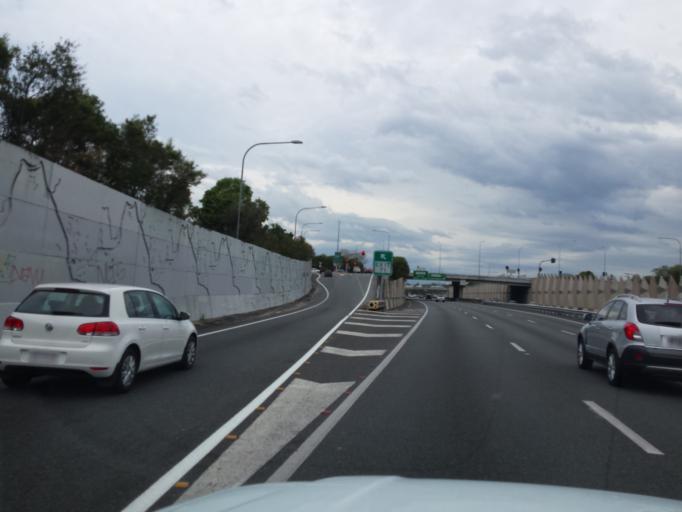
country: AU
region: Queensland
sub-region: Gold Coast
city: Nerang
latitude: -27.9918
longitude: 153.3404
